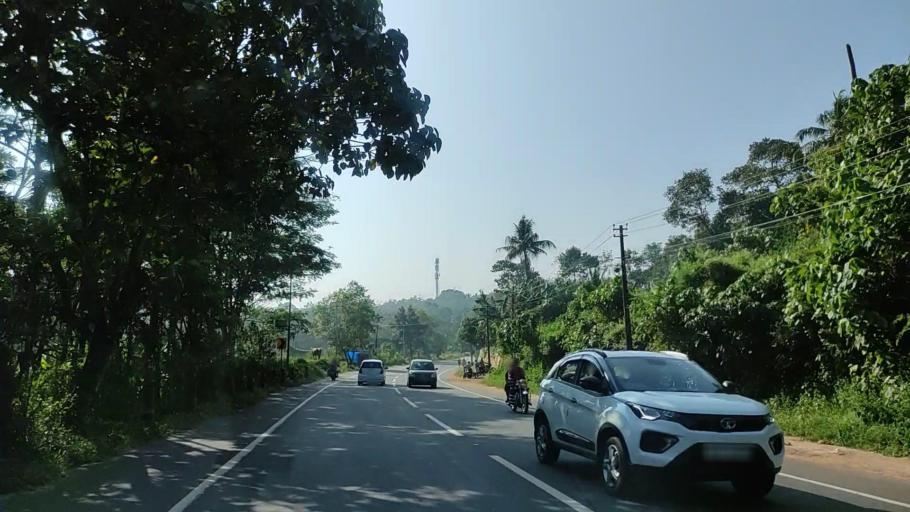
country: IN
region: Kerala
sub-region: Kollam
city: Punalur
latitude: 8.9112
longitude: 76.8547
